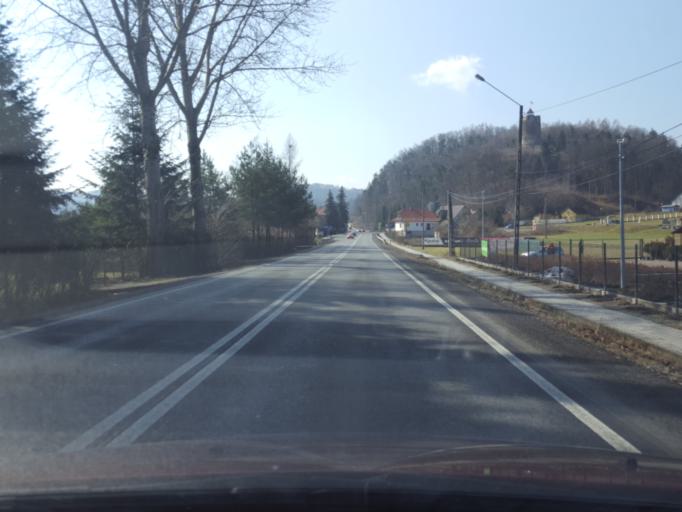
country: PL
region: Lesser Poland Voivodeship
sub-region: Powiat brzeski
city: Czchow
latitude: 49.8364
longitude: 20.6801
